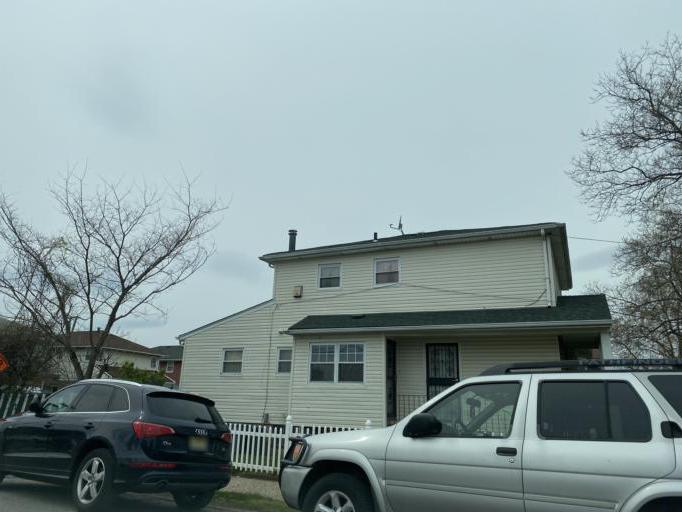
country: US
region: New York
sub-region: Queens County
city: Jamaica
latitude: 40.6691
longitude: -73.7780
